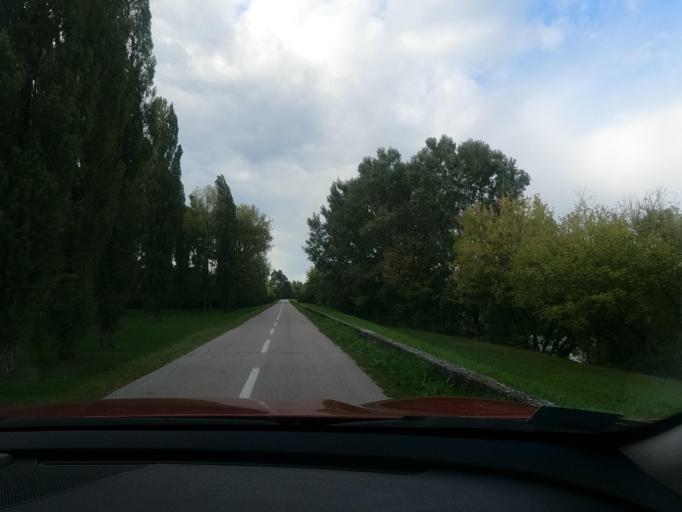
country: HR
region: Sisacko-Moslavacka
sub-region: Grad Sisak
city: Sisak
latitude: 45.4736
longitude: 16.3849
